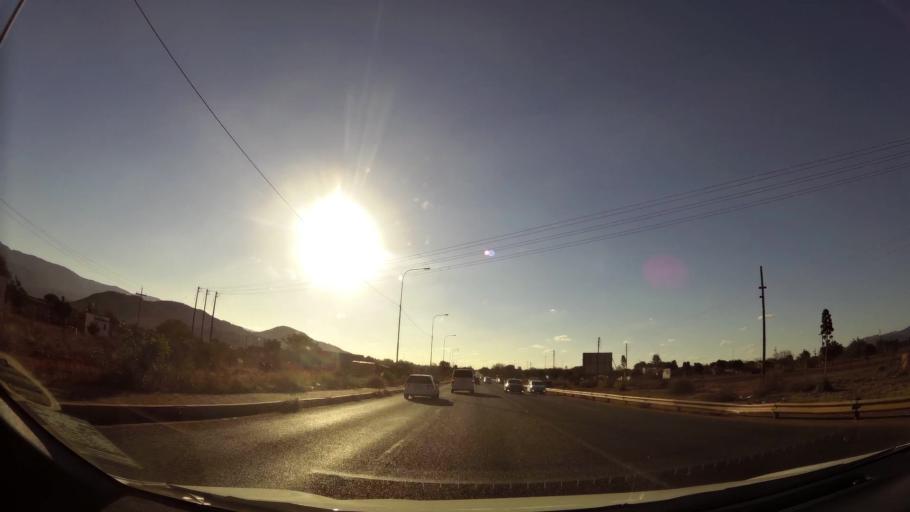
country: ZA
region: Limpopo
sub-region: Waterberg District Municipality
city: Mokopane
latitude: -24.1610
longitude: 28.9899
